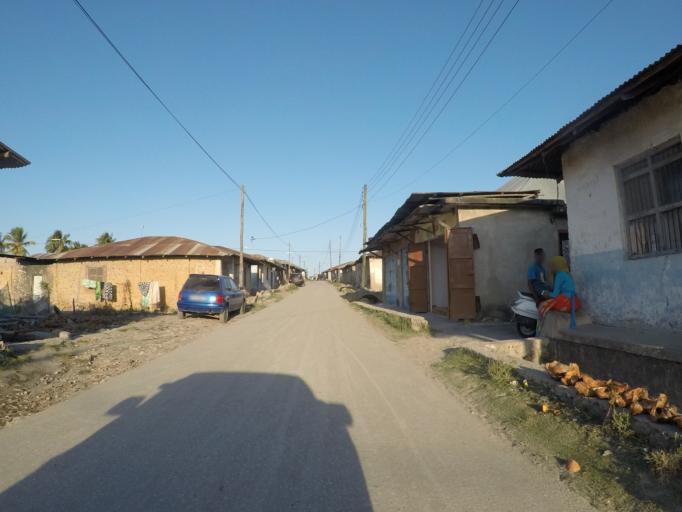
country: TZ
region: Zanzibar Urban/West
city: Zanzibar
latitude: -6.1576
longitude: 39.2109
